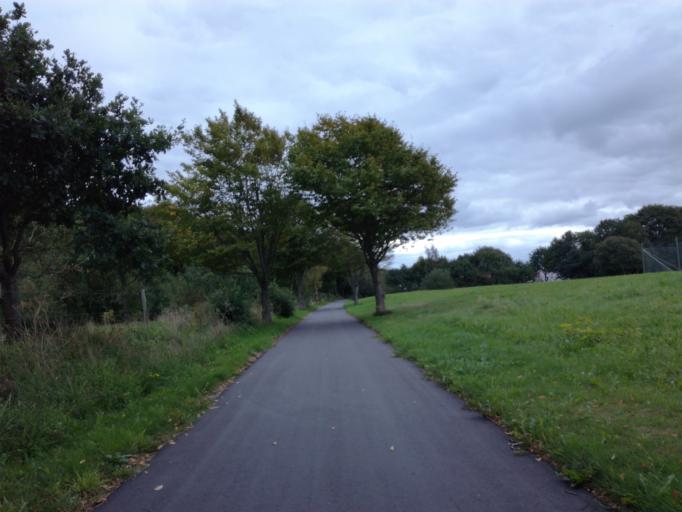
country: DK
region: South Denmark
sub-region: Vejle Kommune
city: Vejle
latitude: 55.6842
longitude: 9.5756
